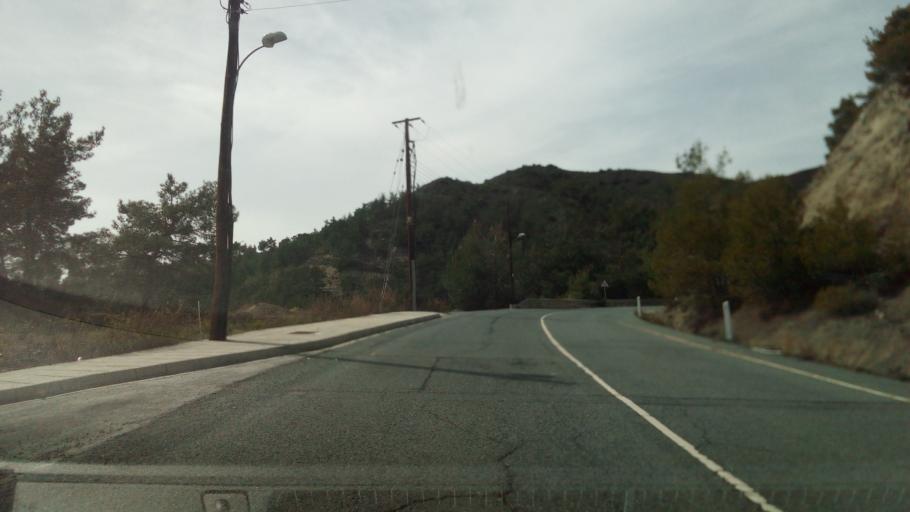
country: CY
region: Limassol
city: Pelendri
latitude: 34.8901
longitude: 32.9573
